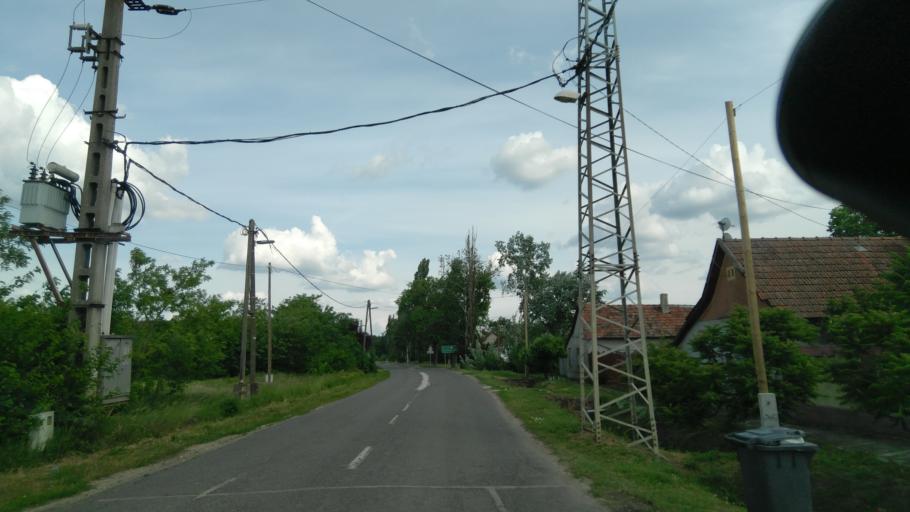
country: HU
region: Bekes
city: Battonya
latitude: 46.2821
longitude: 21.0414
